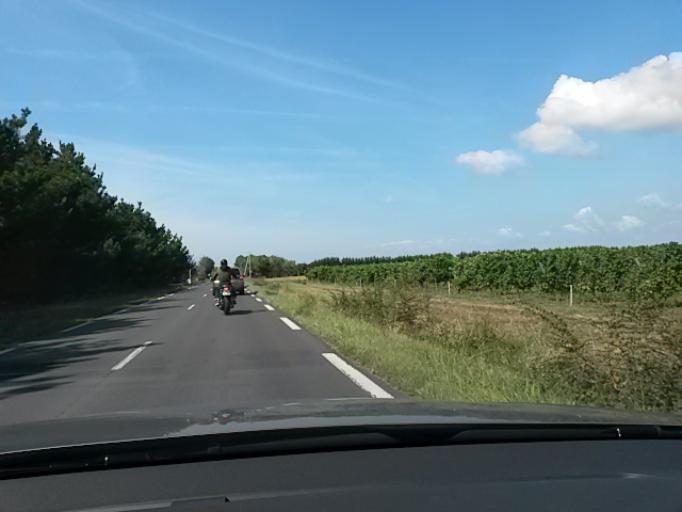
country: FR
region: Poitou-Charentes
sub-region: Departement de la Charente-Maritime
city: Saint-Denis-d'Oleron
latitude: 45.9627
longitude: -1.3436
